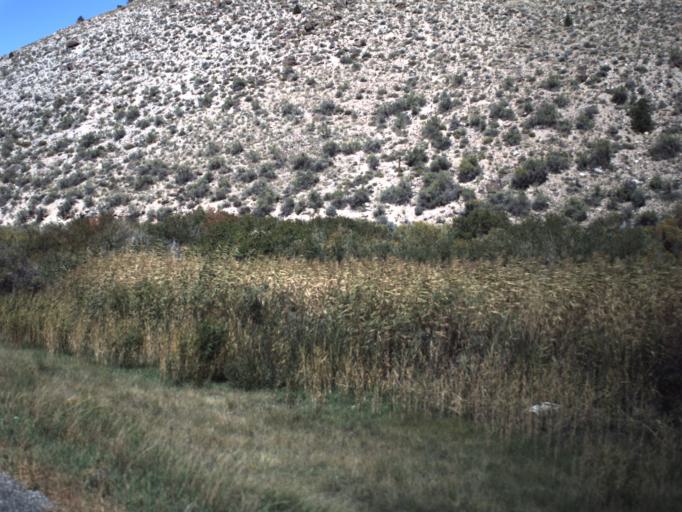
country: US
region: Utah
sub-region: Piute County
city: Junction
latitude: 38.1845
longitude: -112.0846
